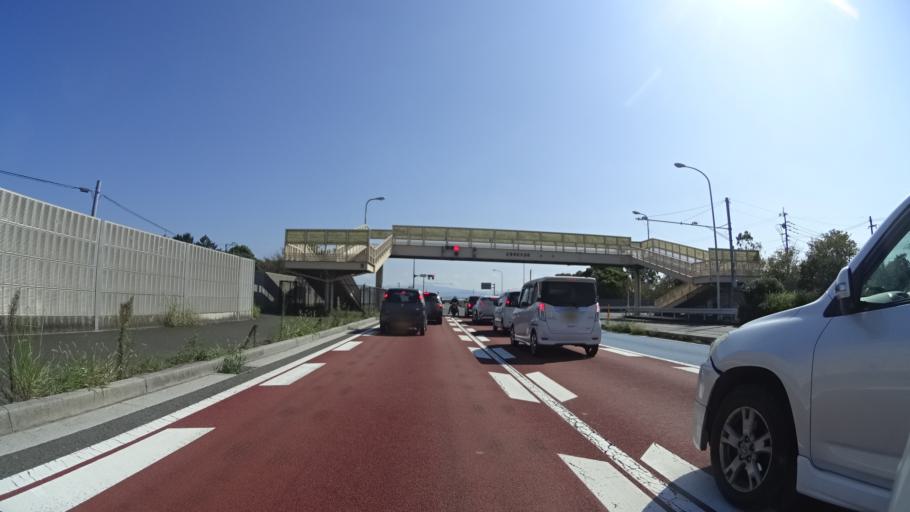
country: JP
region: Fukuoka
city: Yukuhashi
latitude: 33.7266
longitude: 130.9928
